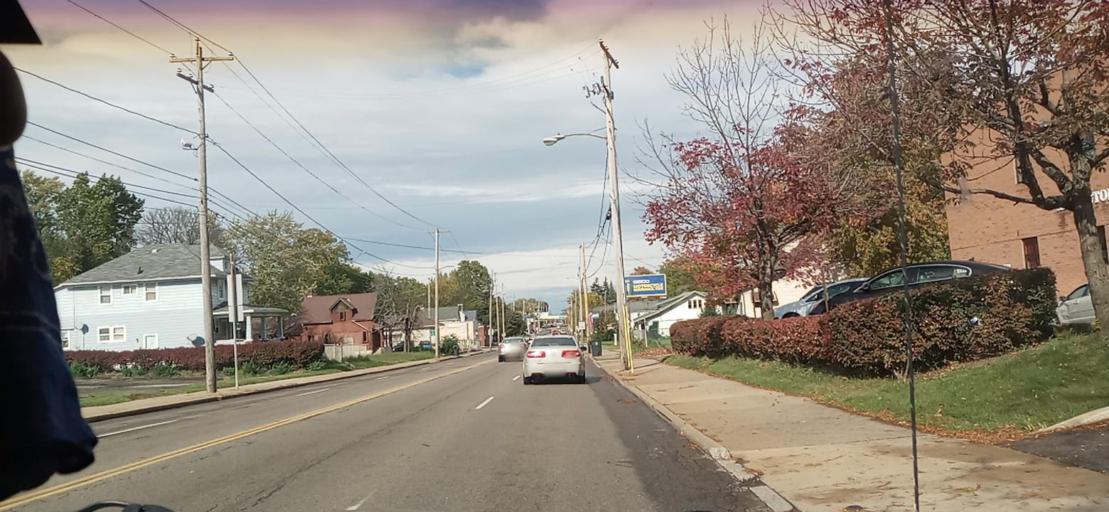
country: US
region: Ohio
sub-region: Summit County
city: Akron
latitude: 41.0580
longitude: -81.4908
